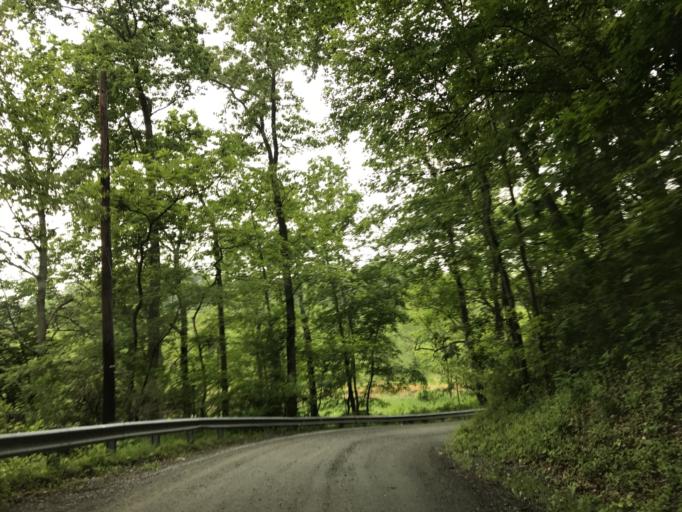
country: US
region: Maryland
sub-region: Harford County
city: Jarrettsville
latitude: 39.6759
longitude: -76.4537
